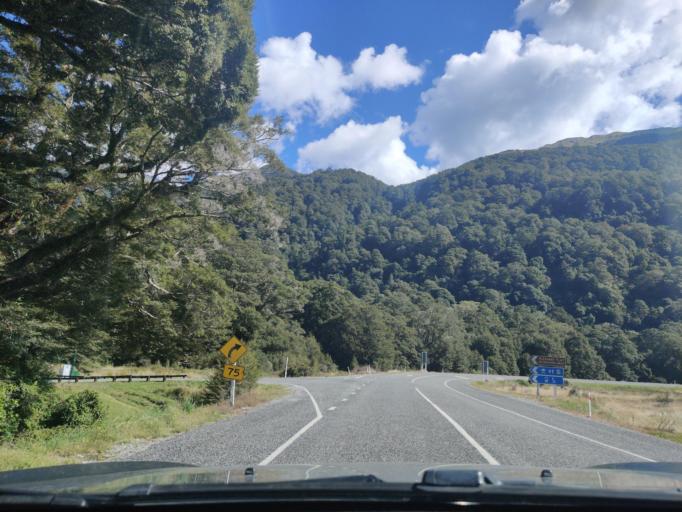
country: NZ
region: Otago
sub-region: Queenstown-Lakes District
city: Wanaka
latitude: -44.0118
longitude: 169.3824
